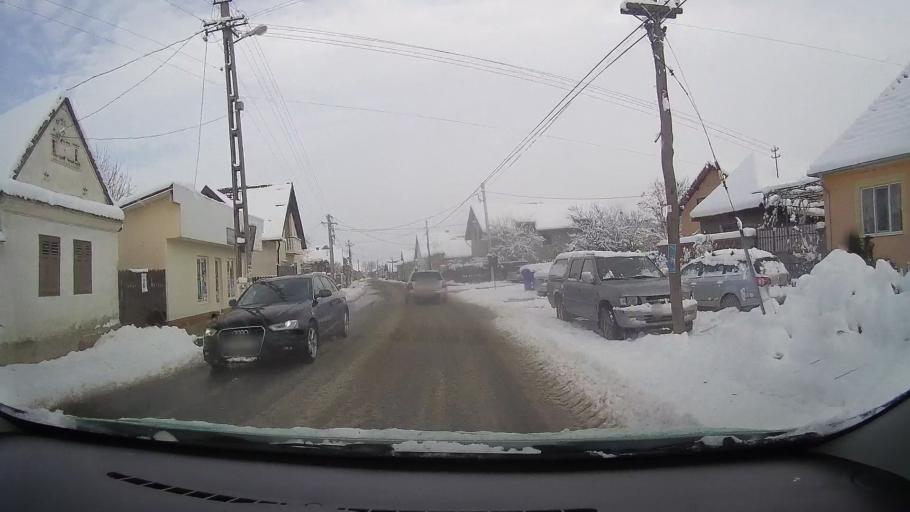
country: RO
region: Alba
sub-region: Comuna Pianu
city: Pianu de Jos
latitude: 45.9288
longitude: 23.4860
